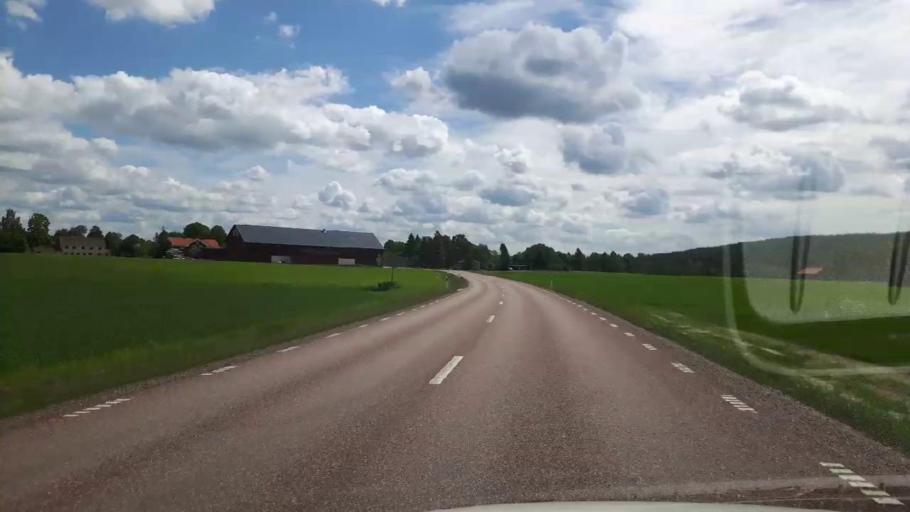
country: SE
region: Dalarna
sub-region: Saters Kommun
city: Saeter
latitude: 60.4000
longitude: 15.8768
